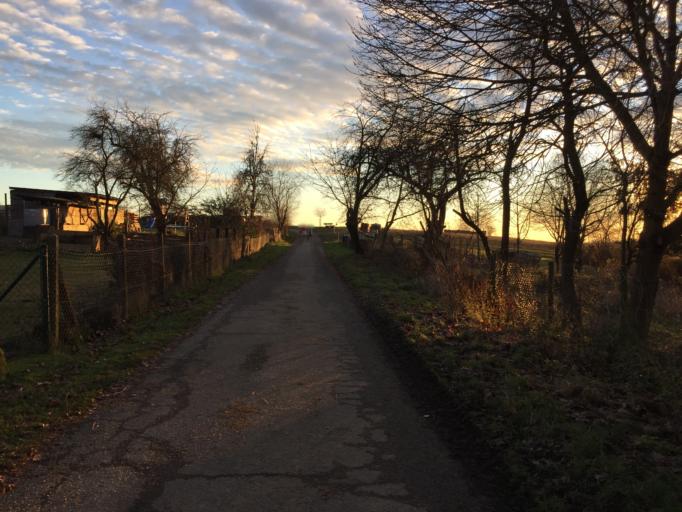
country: DE
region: Rheinland-Pfalz
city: Hardert
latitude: 50.5164
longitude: 7.5196
